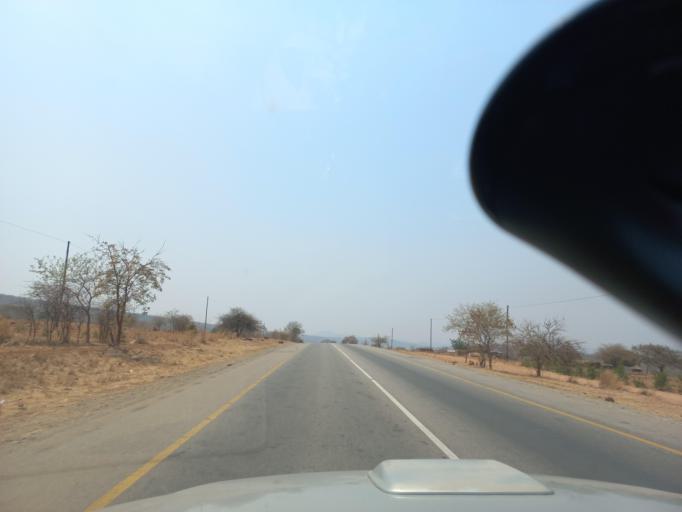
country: ZM
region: Lusaka
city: Kafue
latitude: -15.8840
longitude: 28.3151
